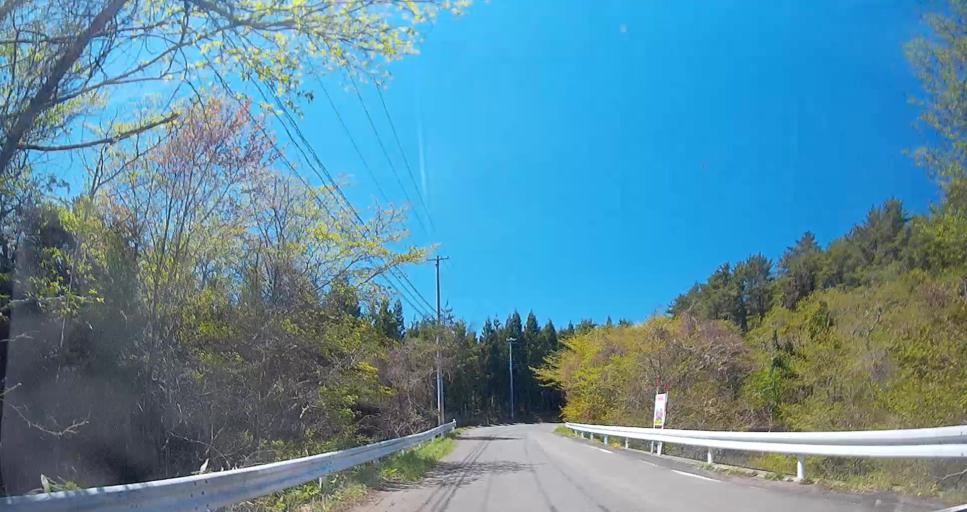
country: JP
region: Aomori
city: Mutsu
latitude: 41.2485
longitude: 141.3948
